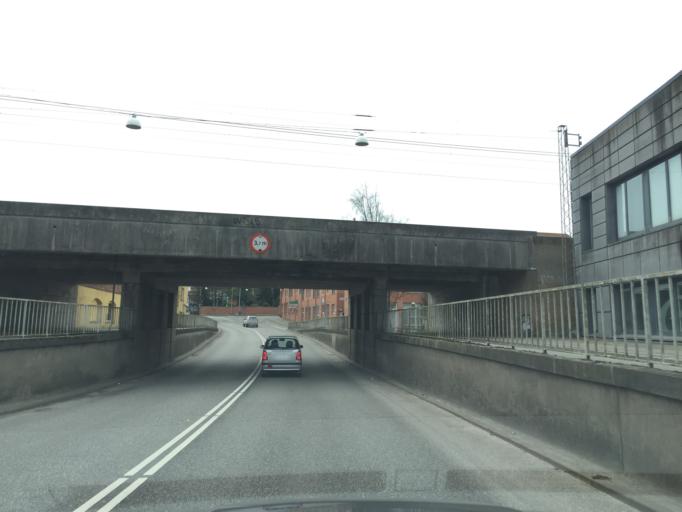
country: DK
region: South Denmark
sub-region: Kolding Kommune
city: Kolding
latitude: 55.4879
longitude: 9.4718
